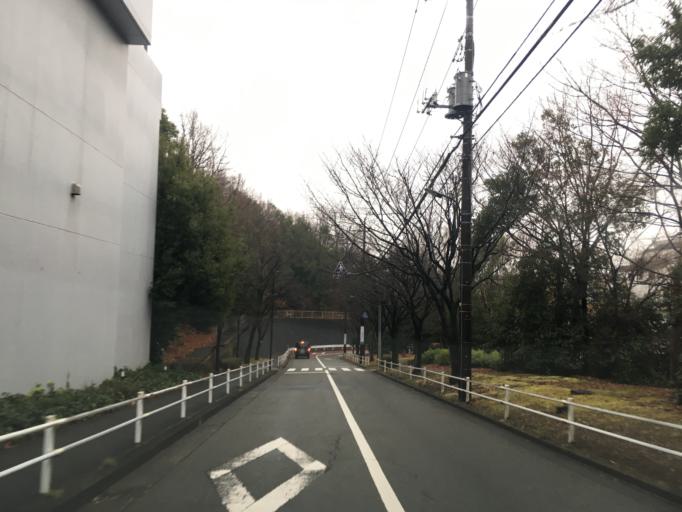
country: JP
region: Tokyo
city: Hino
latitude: 35.6295
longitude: 139.4569
